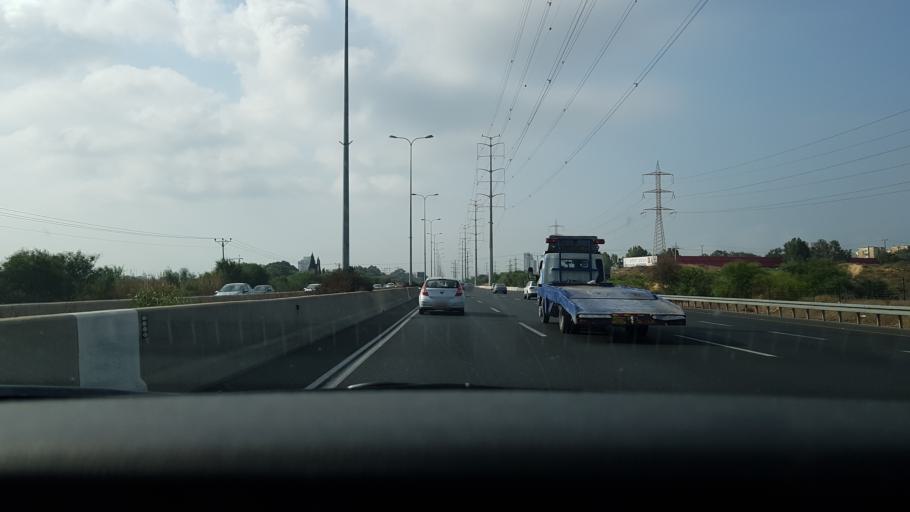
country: IL
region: Central District
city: Rishon LeZiyyon
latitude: 31.9917
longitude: 34.7984
